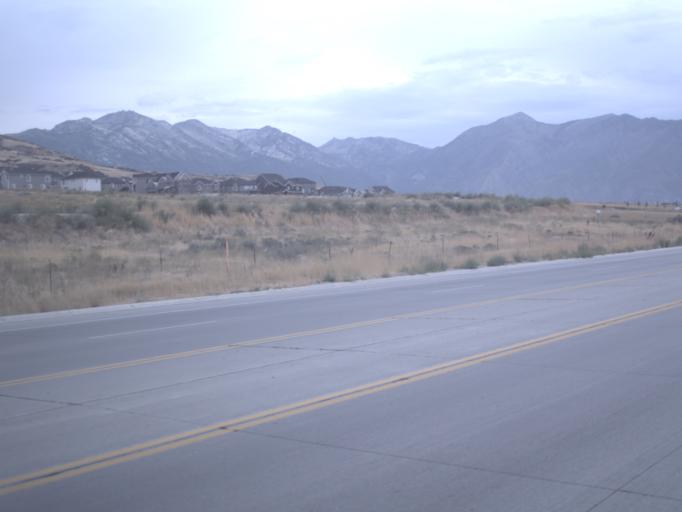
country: US
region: Utah
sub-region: Utah County
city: Lehi
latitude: 40.4326
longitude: -111.8656
